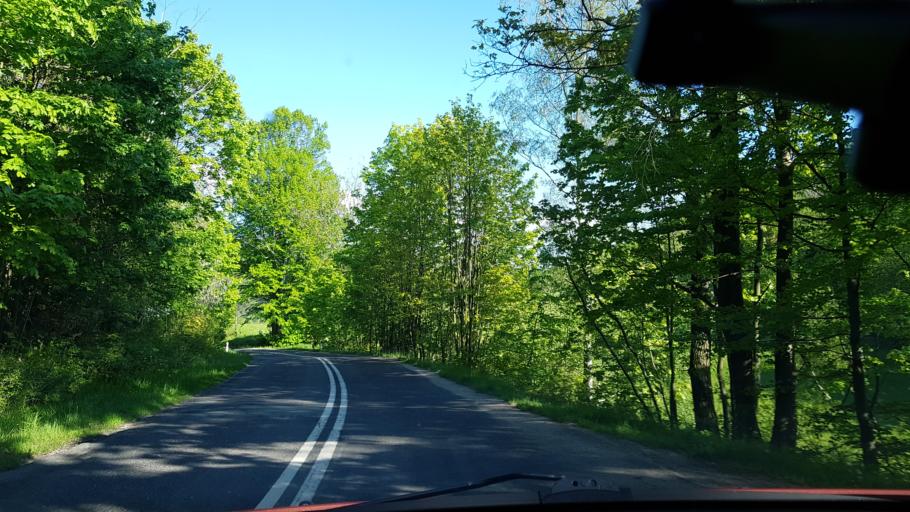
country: PL
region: Lower Silesian Voivodeship
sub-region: Powiat klodzki
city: Bozkow
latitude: 50.5739
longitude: 16.6048
